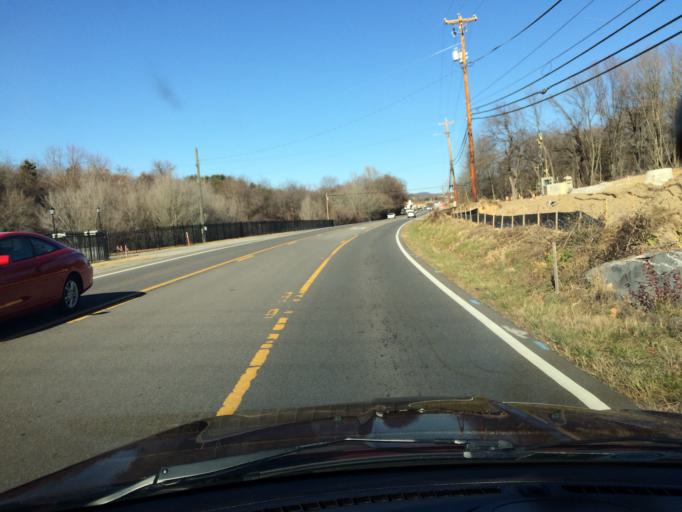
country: US
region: Virginia
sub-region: Roanoke County
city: Hollins
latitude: 37.3397
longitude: -79.9564
